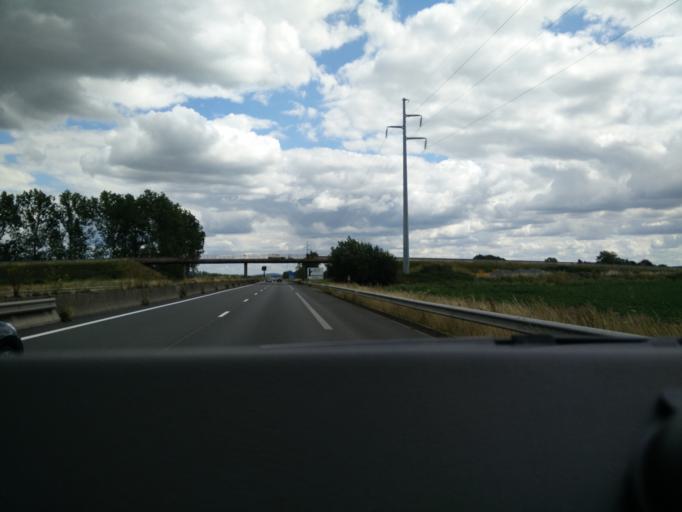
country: FR
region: Nord-Pas-de-Calais
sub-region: Departement du Nord
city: Wormhout
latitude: 50.9035
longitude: 2.4929
